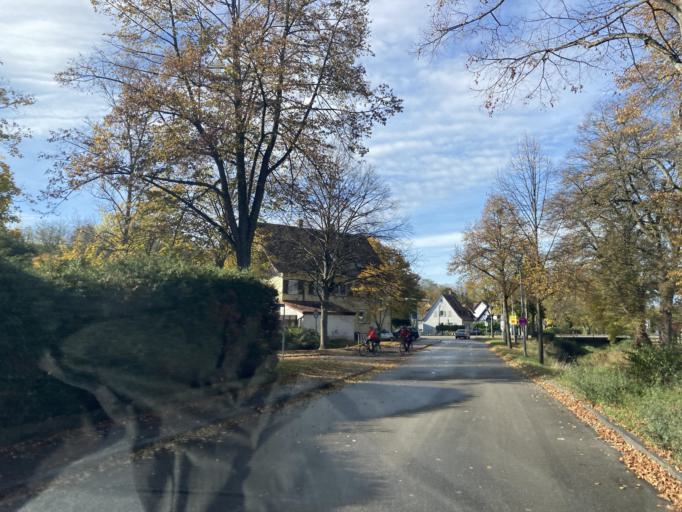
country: DE
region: Baden-Wuerttemberg
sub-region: Freiburg Region
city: Mullheim
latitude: 47.8074
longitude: 7.6200
